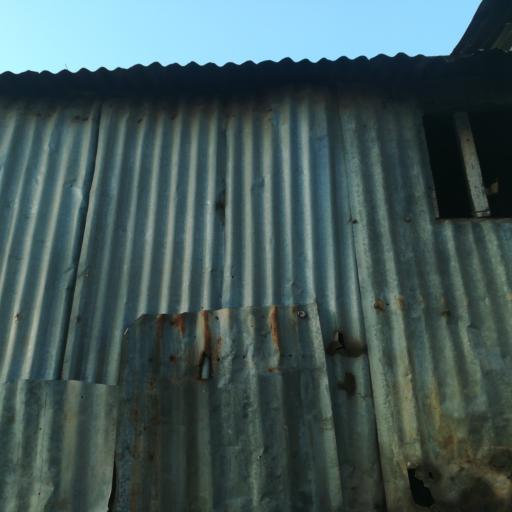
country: NG
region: Kano
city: Kano
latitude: 12.0144
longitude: 8.5041
